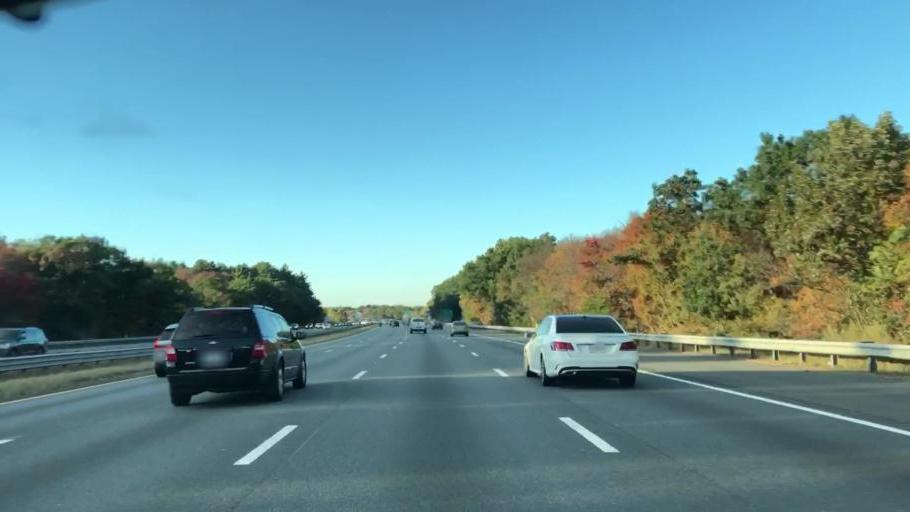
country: US
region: Massachusetts
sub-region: Middlesex County
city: Wilmington
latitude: 42.5439
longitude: -71.1352
